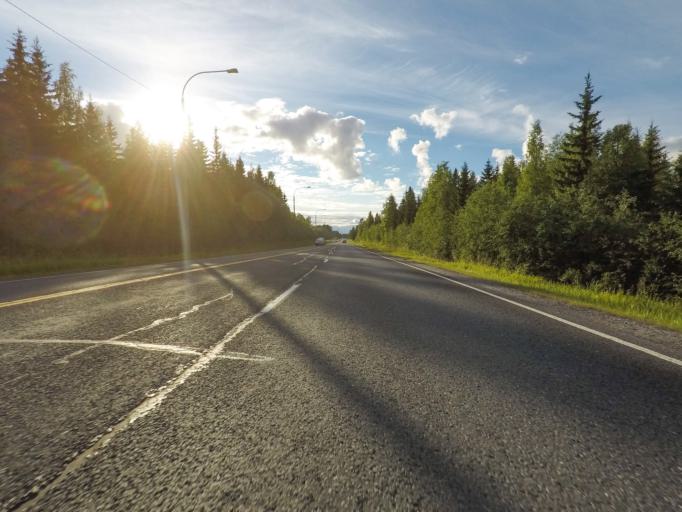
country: FI
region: Northern Savo
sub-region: Kuopio
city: Kuopio
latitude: 62.9487
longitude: 27.8850
